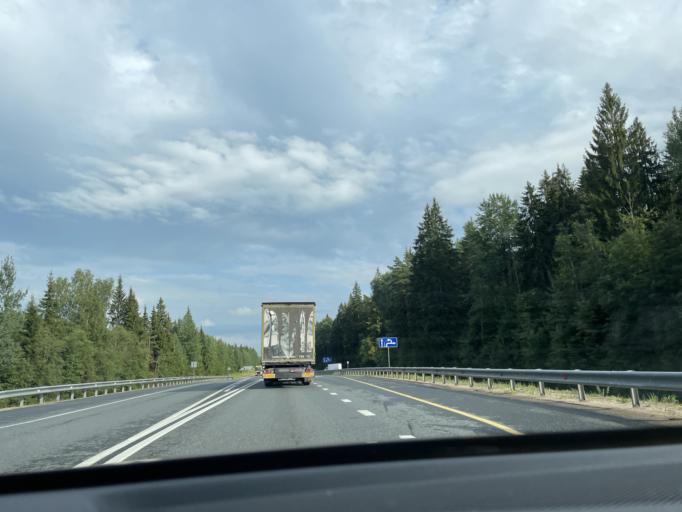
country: RU
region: Tverskaya
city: Kuzhenkino
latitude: 57.7453
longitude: 34.0048
